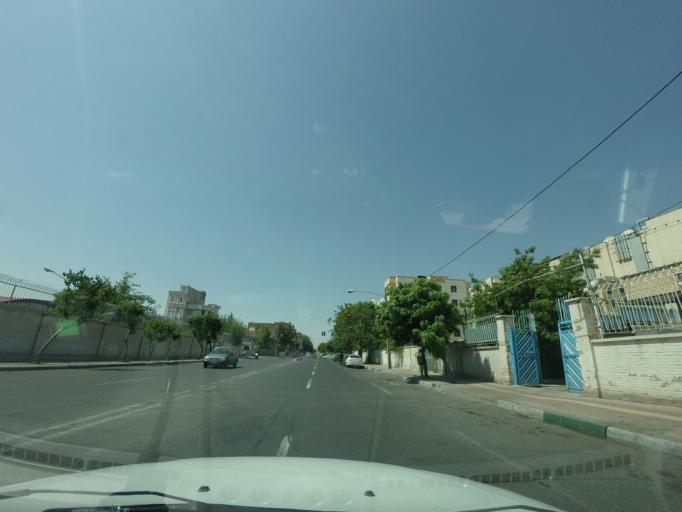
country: IR
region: Tehran
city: Tehran
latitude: 35.6399
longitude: 51.3665
